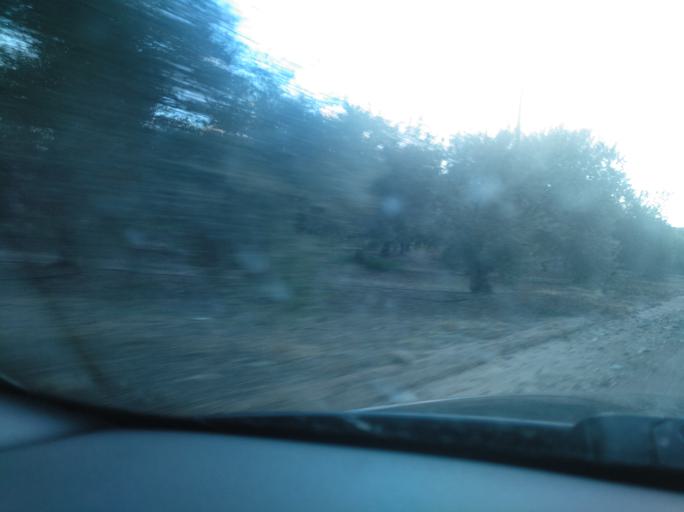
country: PT
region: Portalegre
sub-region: Campo Maior
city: Campo Maior
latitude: 39.0139
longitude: -7.0528
